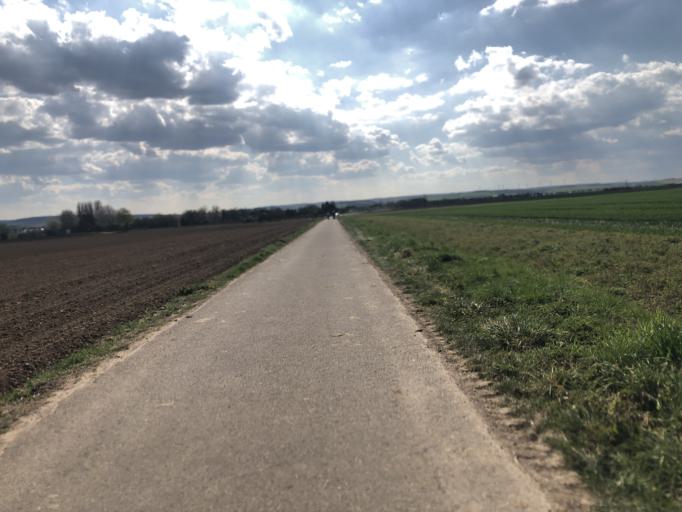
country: DE
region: North Rhine-Westphalia
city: Zulpich
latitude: 50.6769
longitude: 6.6543
